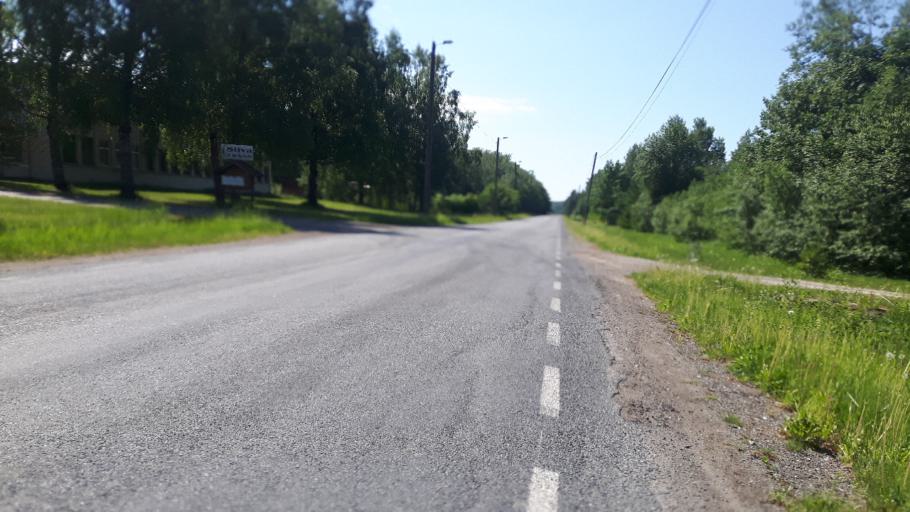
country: EE
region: Paernumaa
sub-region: Vaendra vald (alev)
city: Vandra
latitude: 58.6433
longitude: 25.0273
